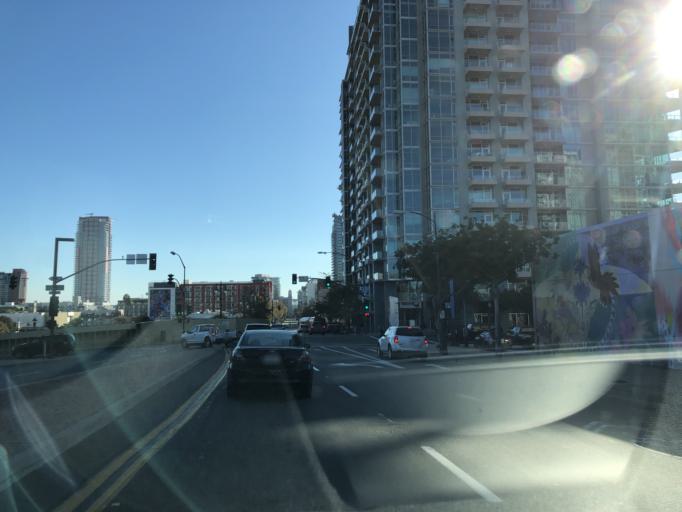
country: US
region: California
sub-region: San Diego County
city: San Diego
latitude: 32.7173
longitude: -117.1538
